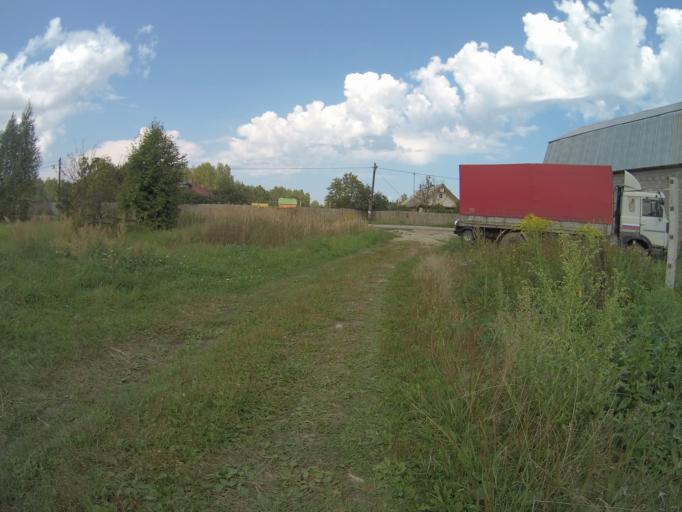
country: RU
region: Vladimir
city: Raduzhnyy
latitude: 56.0018
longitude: 40.2846
